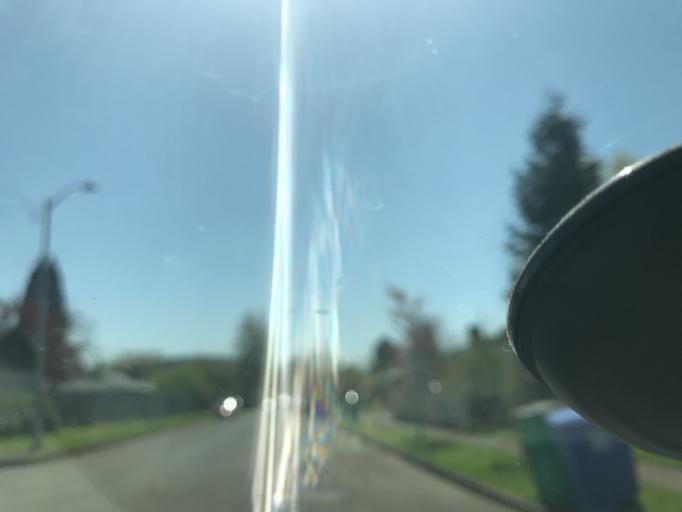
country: US
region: Oregon
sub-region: Multnomah County
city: Lents
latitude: 45.4927
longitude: -122.5572
